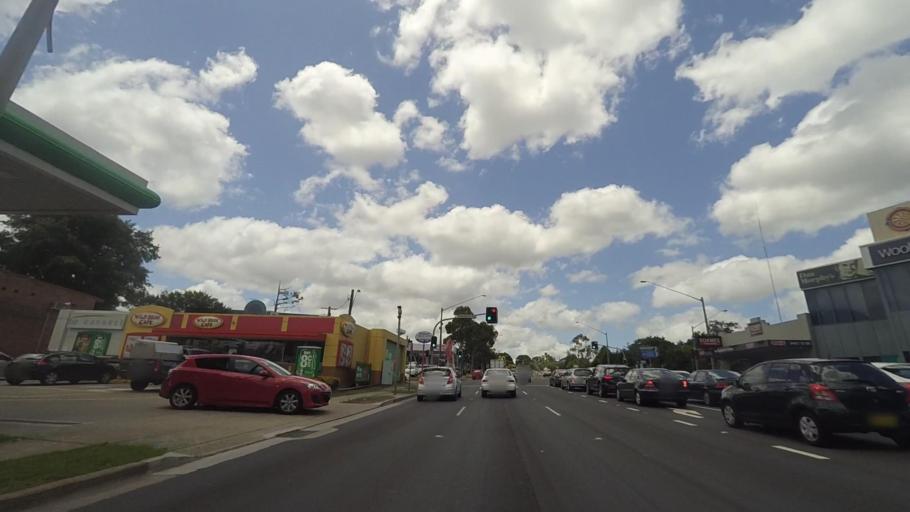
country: AU
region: New South Wales
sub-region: Hornsby Shire
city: Pennant Hills
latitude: -33.7312
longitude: 151.0806
